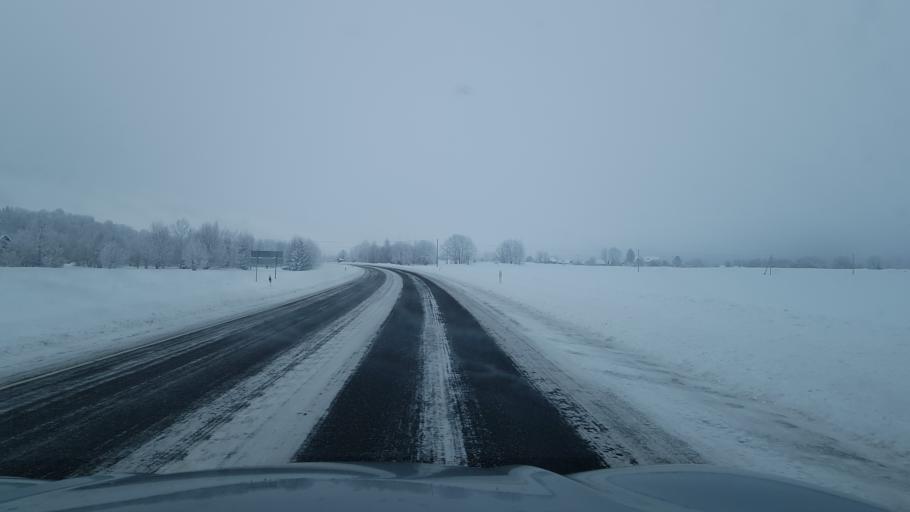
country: EE
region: Ida-Virumaa
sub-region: Johvi vald
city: Johvi
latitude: 59.2533
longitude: 27.3802
